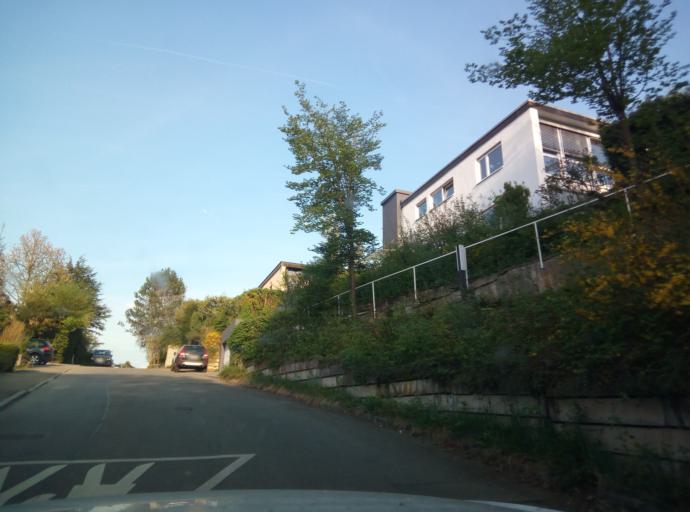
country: DE
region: Baden-Wuerttemberg
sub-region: Tuebingen Region
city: Tuebingen
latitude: 48.5079
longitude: 9.0697
